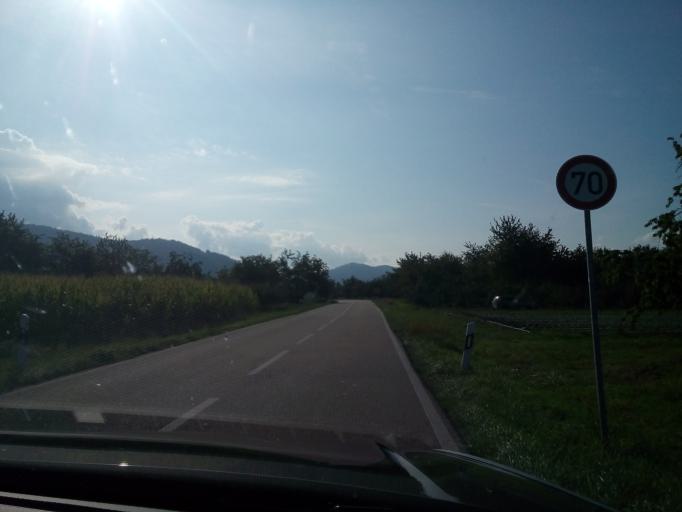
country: DE
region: Baden-Wuerttemberg
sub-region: Freiburg Region
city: Haslach
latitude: 48.5490
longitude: 8.0598
